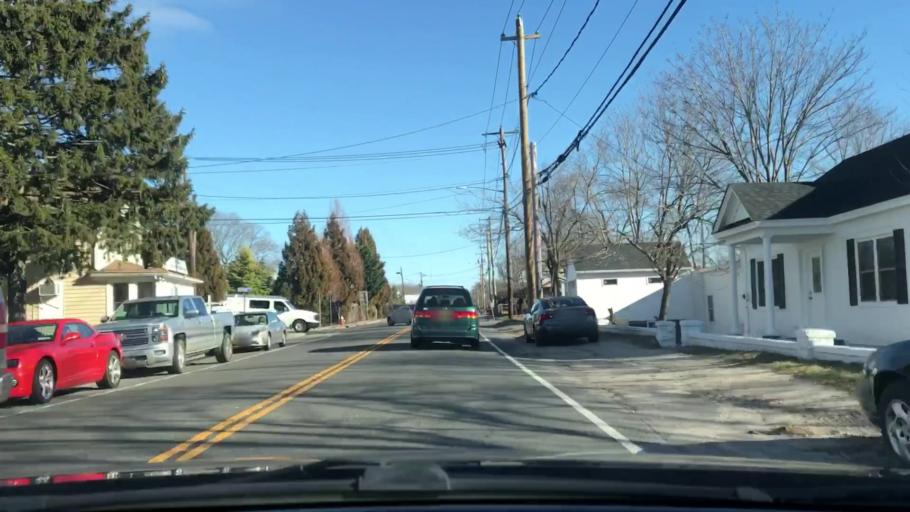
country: US
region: New York
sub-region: Suffolk County
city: Riverhead
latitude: 40.9180
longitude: -72.6765
